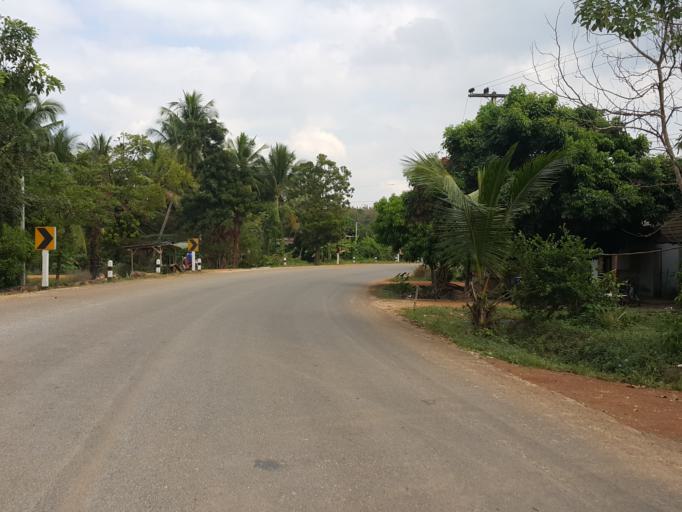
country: TH
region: Sukhothai
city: Thung Saliam
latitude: 17.4519
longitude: 99.6099
